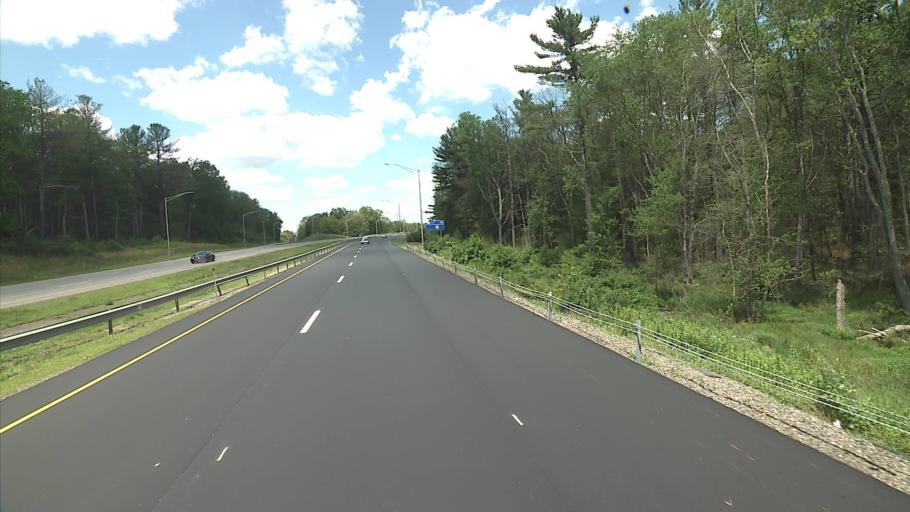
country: US
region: Connecticut
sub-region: Windham County
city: Danielson
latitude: 41.7890
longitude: -71.8746
